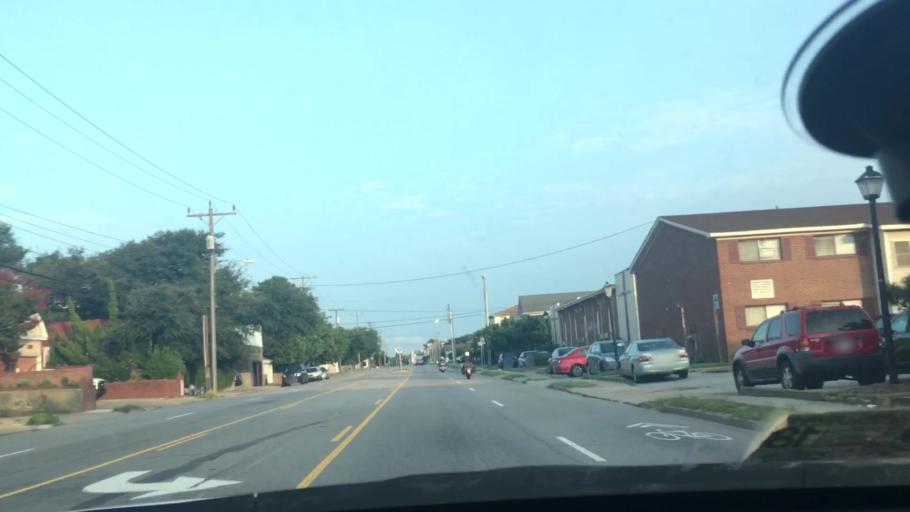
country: US
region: Virginia
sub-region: City of Norfolk
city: Norfolk
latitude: 36.9447
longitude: -76.2366
